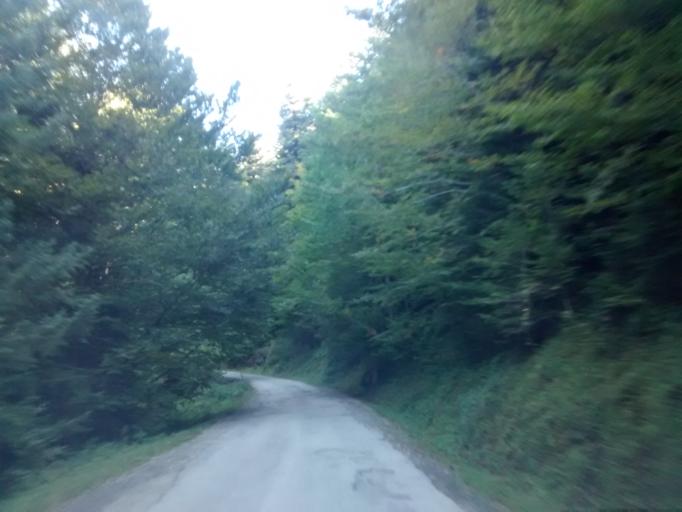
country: ES
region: Aragon
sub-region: Provincia de Huesca
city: Aragues del Puerto
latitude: 42.8421
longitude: -0.7107
